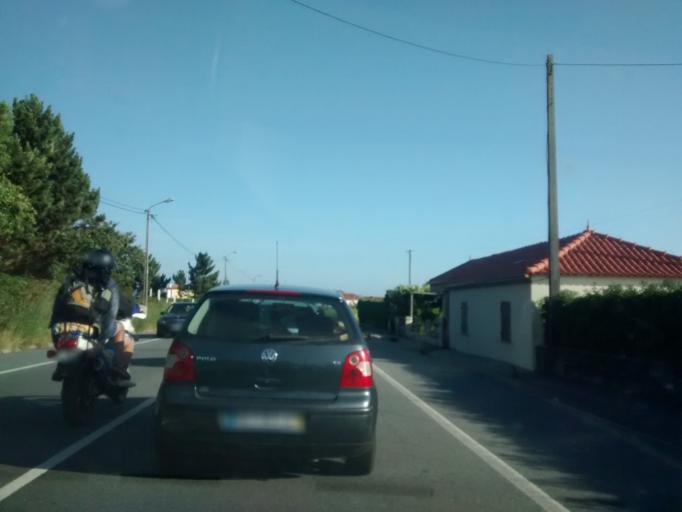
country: PT
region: Viana do Castelo
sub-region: Viana do Castelo
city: Areosa
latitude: 41.7369
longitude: -8.8630
